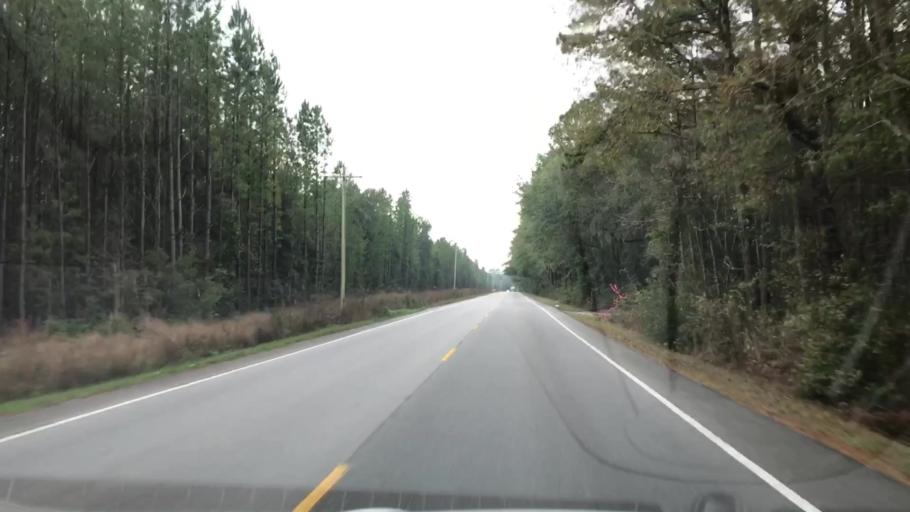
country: US
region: South Carolina
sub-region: Jasper County
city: Ridgeland
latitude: 32.5038
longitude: -80.8867
